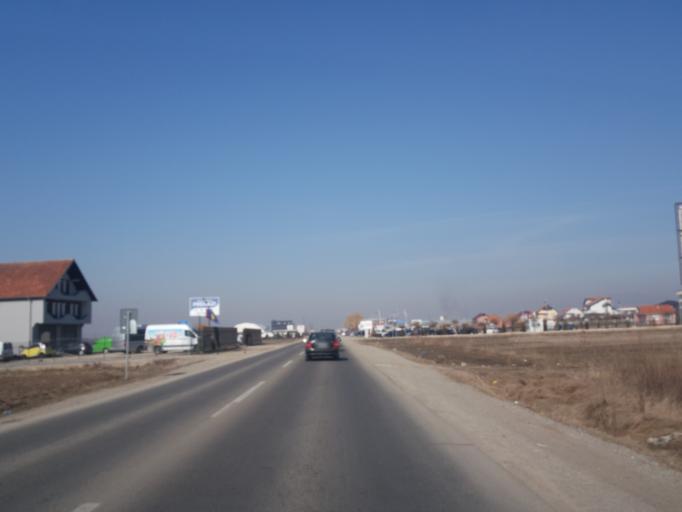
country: XK
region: Mitrovica
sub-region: Vushtrri
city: Vushtrri
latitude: 42.7640
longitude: 21.0274
